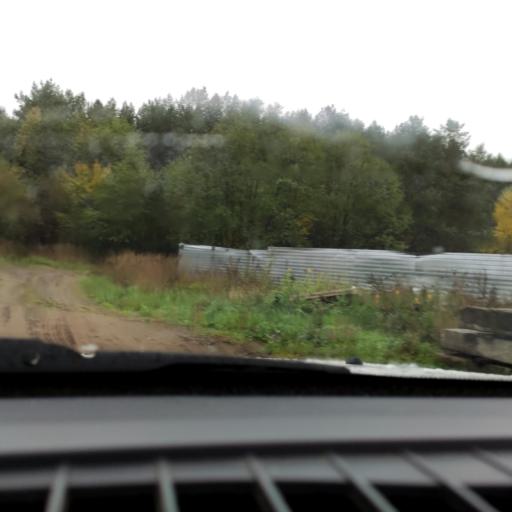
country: RU
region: Perm
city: Perm
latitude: 58.0386
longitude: 56.2565
